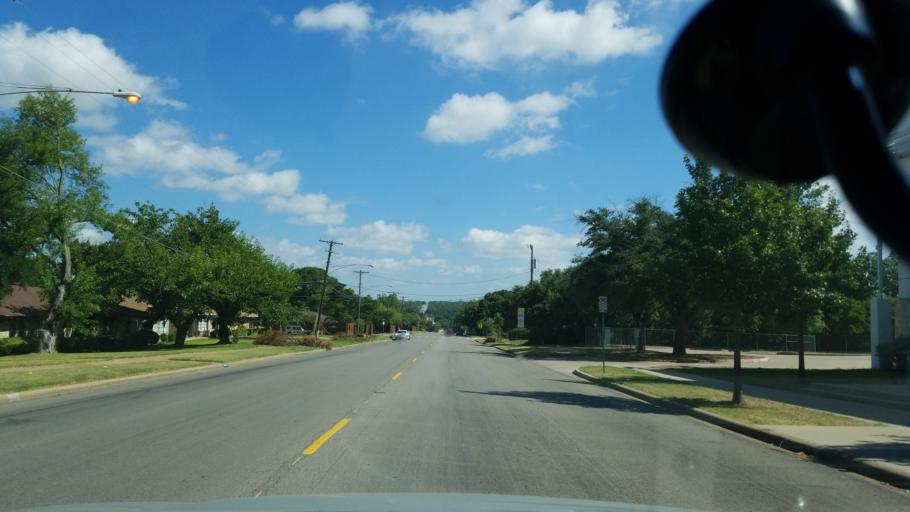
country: US
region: Texas
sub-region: Dallas County
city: Cockrell Hill
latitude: 32.6783
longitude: -96.8147
